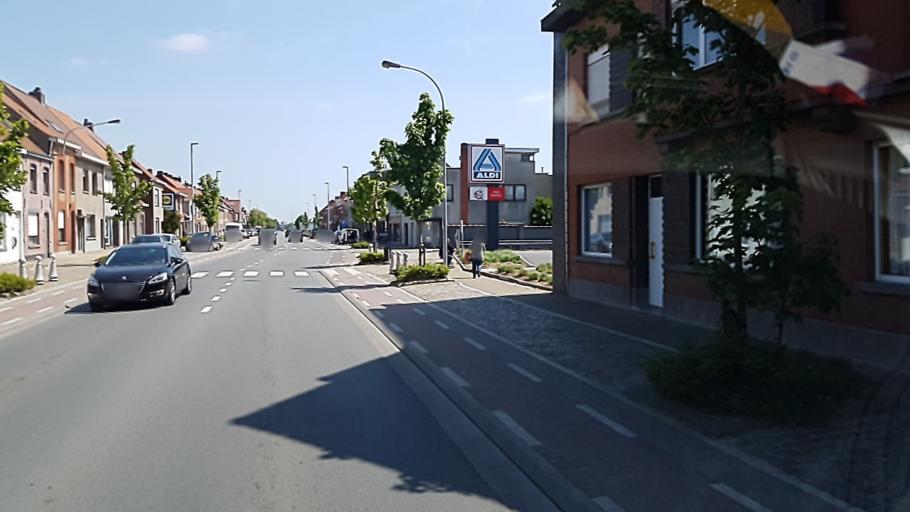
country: FR
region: Nord-Pas-de-Calais
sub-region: Departement du Nord
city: Bousbecque
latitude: 50.8096
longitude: 3.0801
